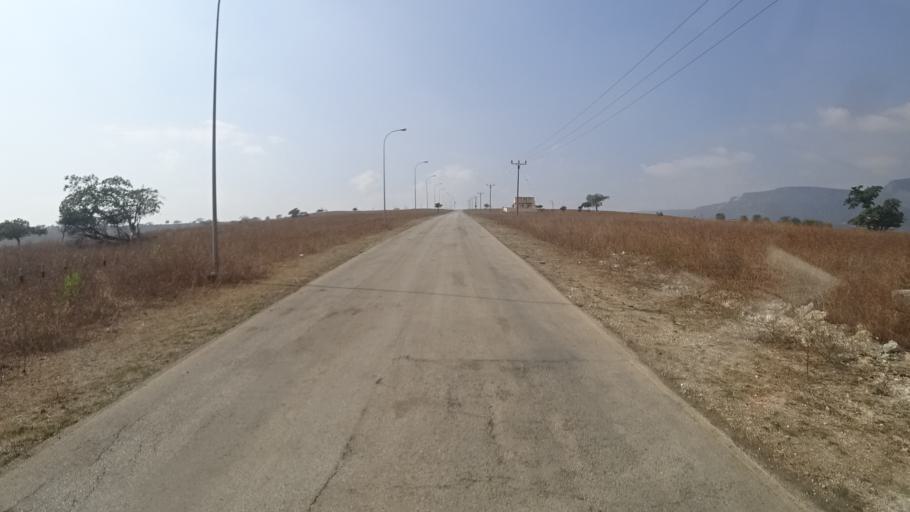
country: YE
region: Al Mahrah
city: Hawf
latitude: 16.7301
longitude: 53.2697
